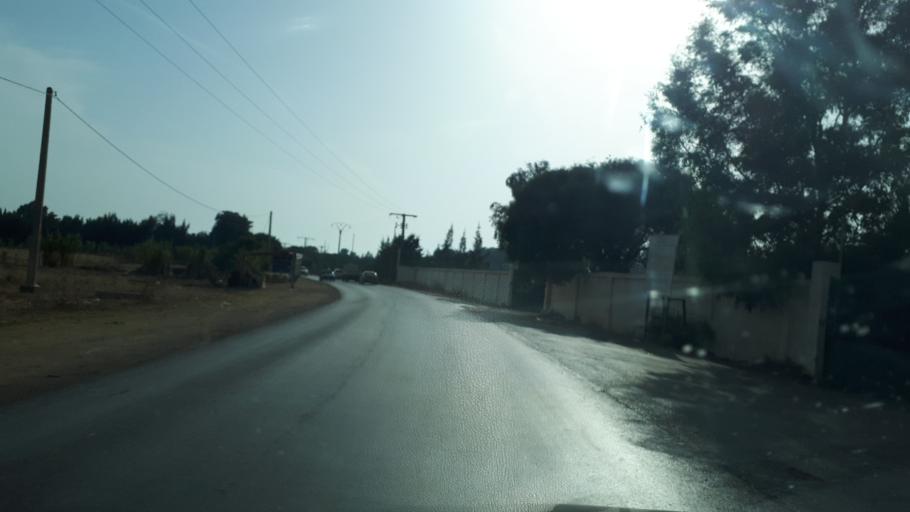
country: DZ
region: Tipaza
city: Zeralda
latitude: 36.7338
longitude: 2.9035
